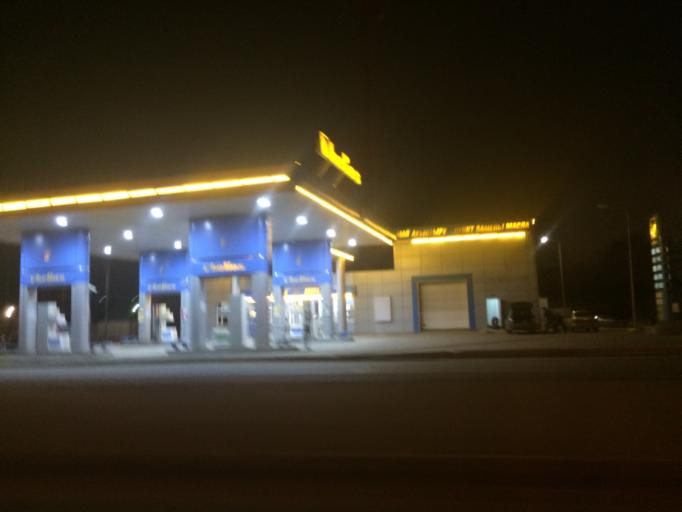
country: KZ
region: Astana Qalasy
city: Astana
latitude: 51.1876
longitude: 71.4513
